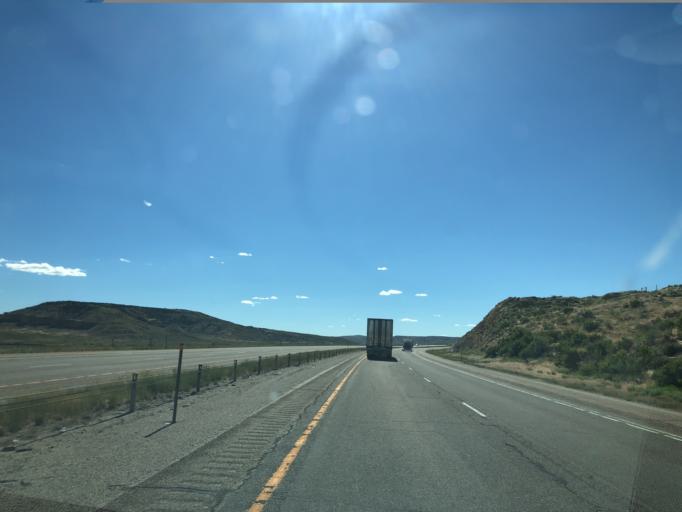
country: US
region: Wyoming
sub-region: Sweetwater County
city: Rock Springs
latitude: 41.6880
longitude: -108.8359
